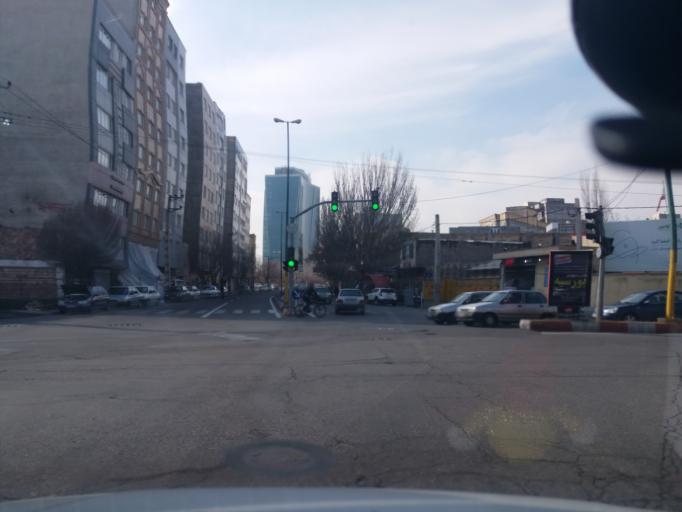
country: IR
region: East Azerbaijan
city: Tabriz
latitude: 38.0369
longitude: 46.3663
